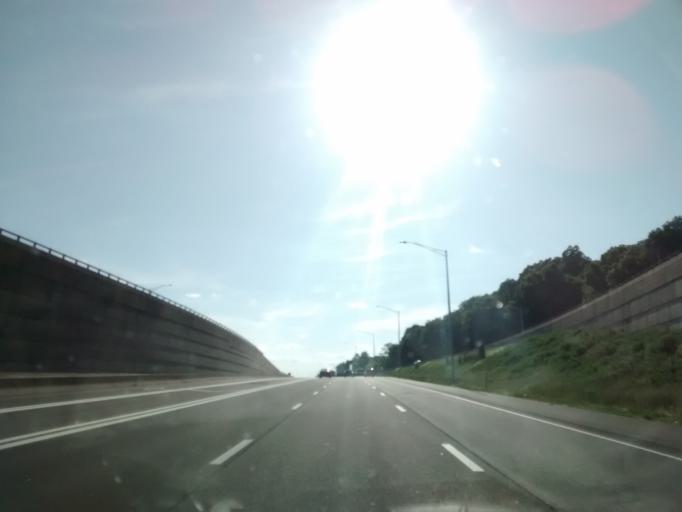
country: US
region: Connecticut
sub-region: Hartford County
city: East Hartford
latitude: 41.7736
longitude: -72.5844
